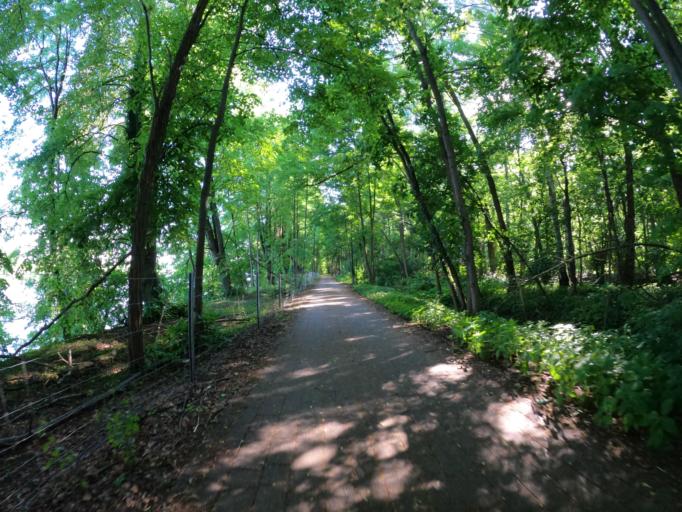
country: DE
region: Brandenburg
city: Gartz
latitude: 53.2261
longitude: 14.4103
